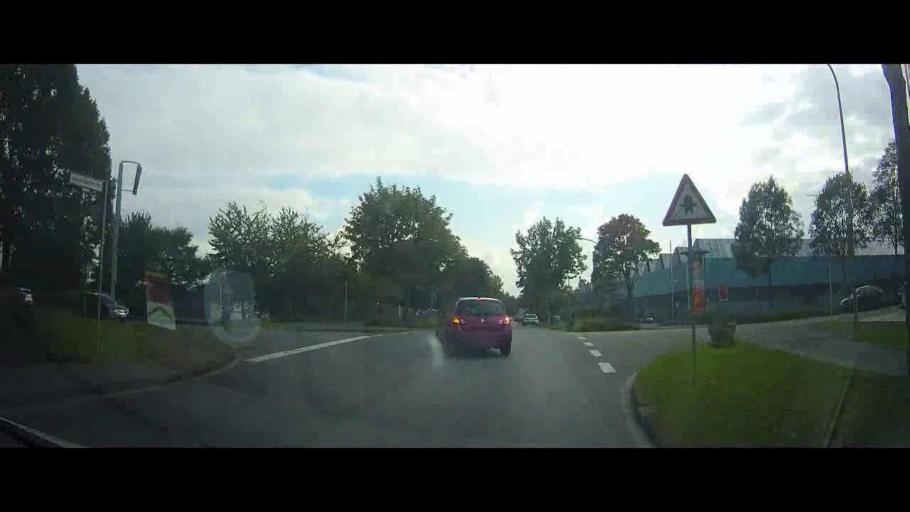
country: DE
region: Lower Saxony
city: Goettingen
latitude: 51.5507
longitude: 9.8927
